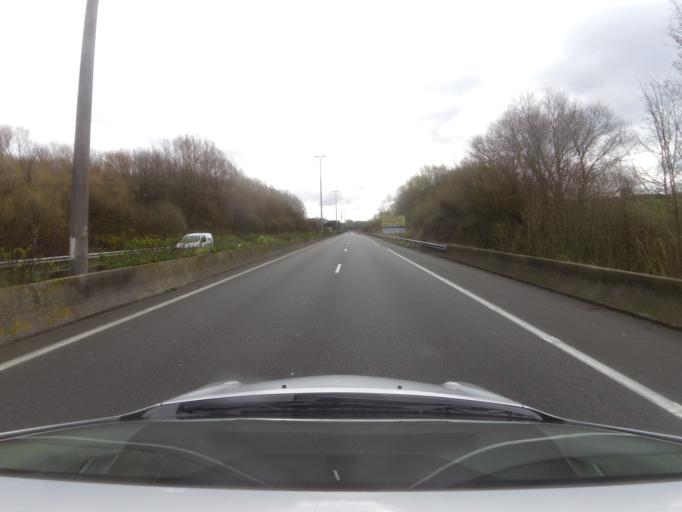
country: FR
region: Nord-Pas-de-Calais
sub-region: Departement du Pas-de-Calais
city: Saint-Martin-Boulogne
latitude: 50.7355
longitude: 1.6384
